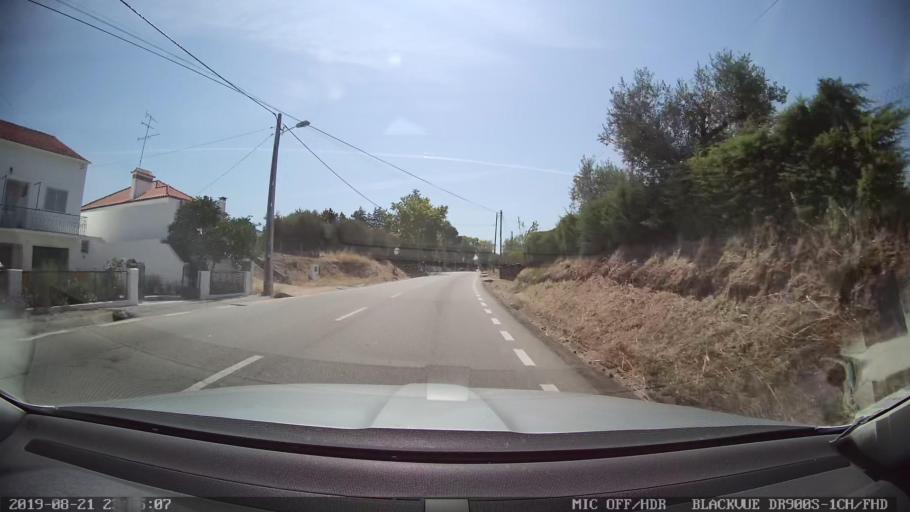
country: PT
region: Castelo Branco
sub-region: Idanha-A-Nova
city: Idanha-a-Nova
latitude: 39.8414
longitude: -7.2679
